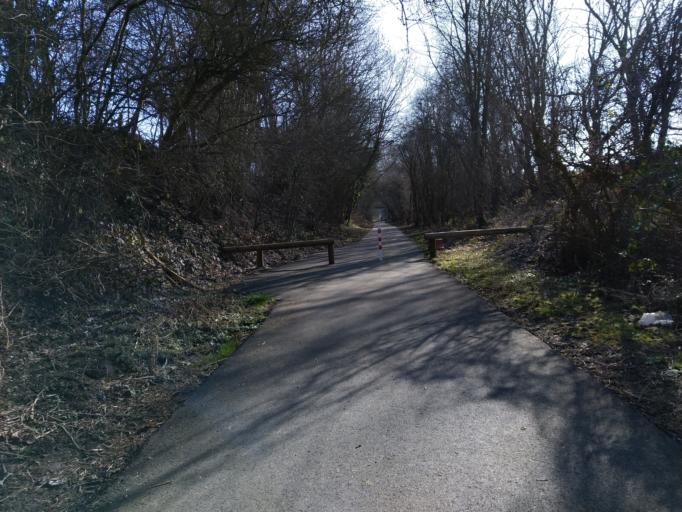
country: BE
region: Wallonia
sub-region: Province du Hainaut
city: Frameries
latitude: 50.4277
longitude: 3.8938
